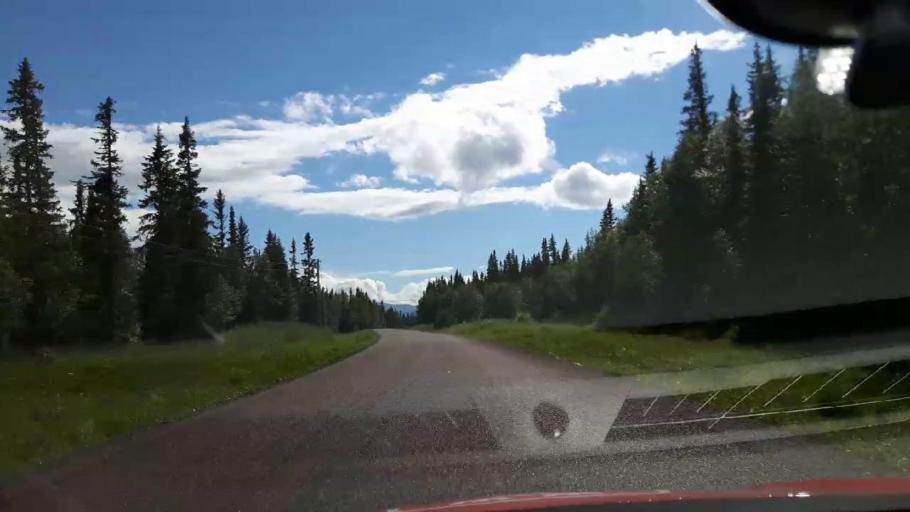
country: SE
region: Jaemtland
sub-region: Are Kommun
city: Are
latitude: 63.2630
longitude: 13.2152
